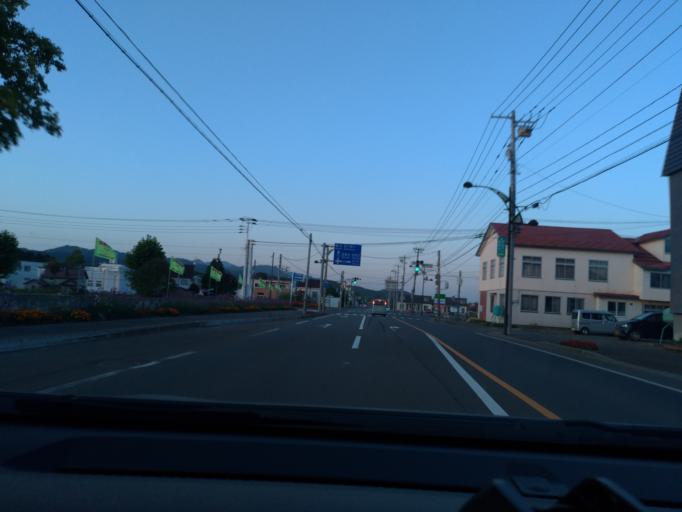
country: JP
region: Hokkaido
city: Iwamizawa
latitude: 43.3386
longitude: 141.6739
